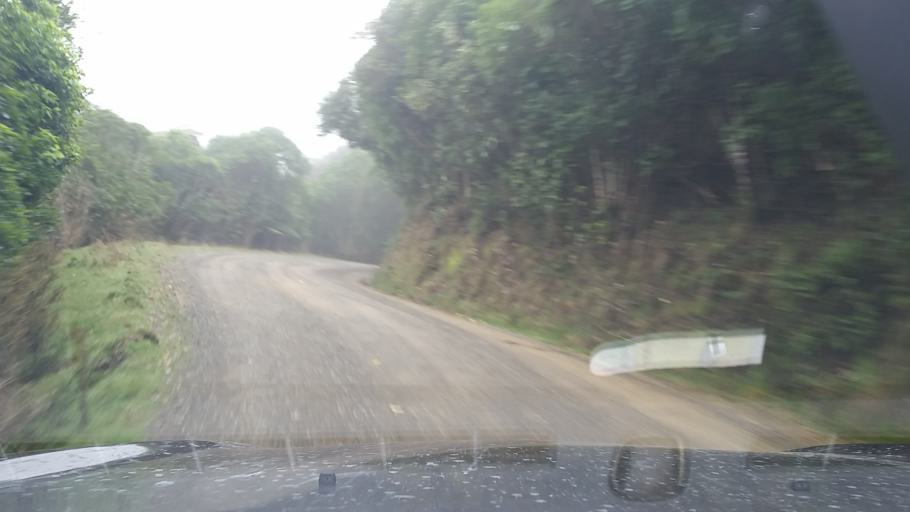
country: NZ
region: Marlborough
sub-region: Marlborough District
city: Picton
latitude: -41.1779
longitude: 173.9817
